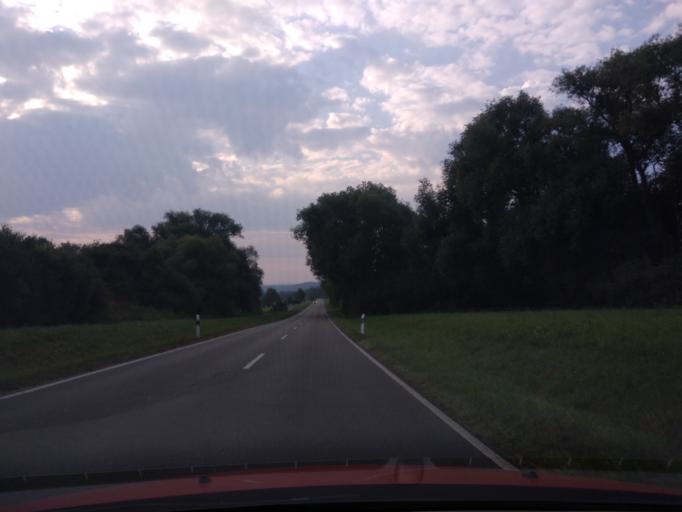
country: DE
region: Hesse
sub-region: Regierungsbezirk Kassel
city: Calden
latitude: 51.3765
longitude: 9.3799
